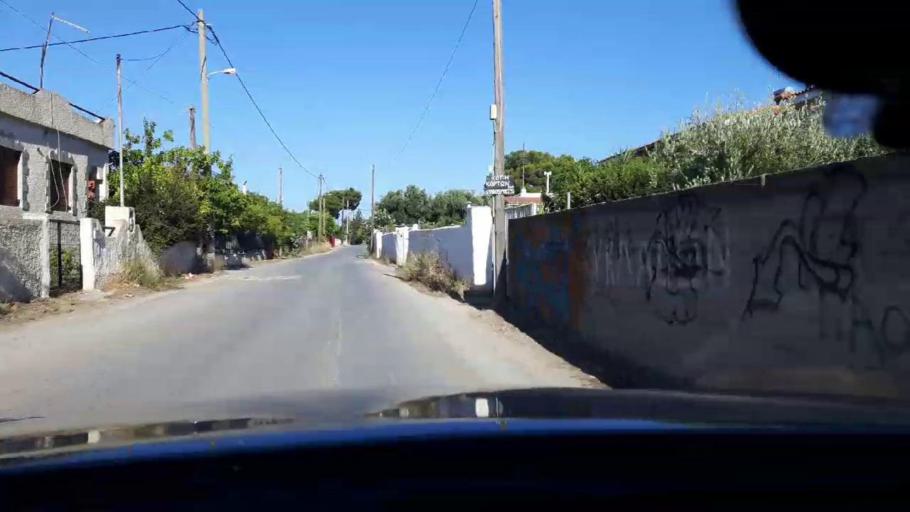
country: GR
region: Attica
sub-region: Nomarchia Anatolikis Attikis
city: Limin Mesoyaias
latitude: 37.8675
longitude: 24.0262
